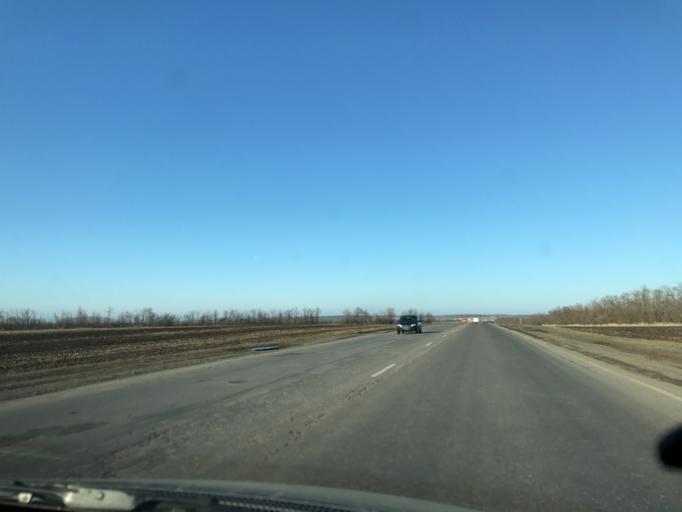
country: RU
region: Rostov
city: Kagal'nitskaya
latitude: 46.8621
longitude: 40.1831
